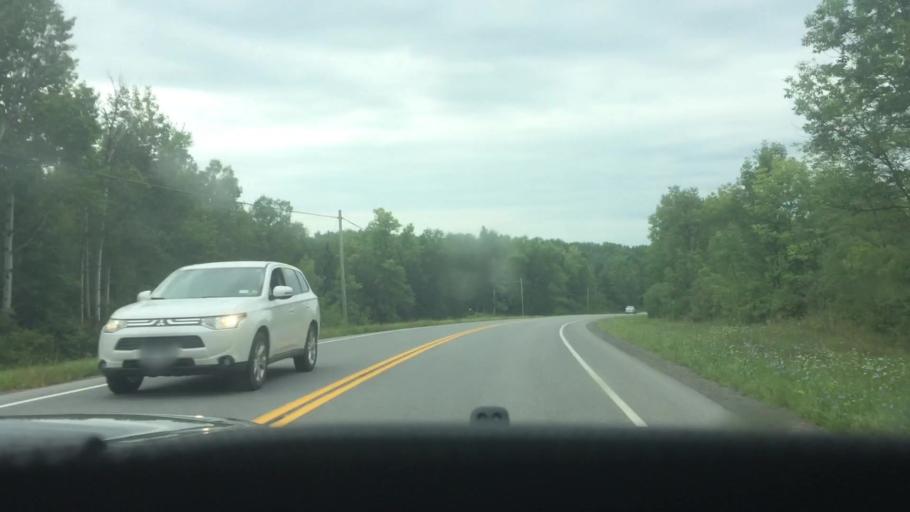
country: US
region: New York
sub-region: St. Lawrence County
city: Canton
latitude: 44.5064
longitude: -75.3401
